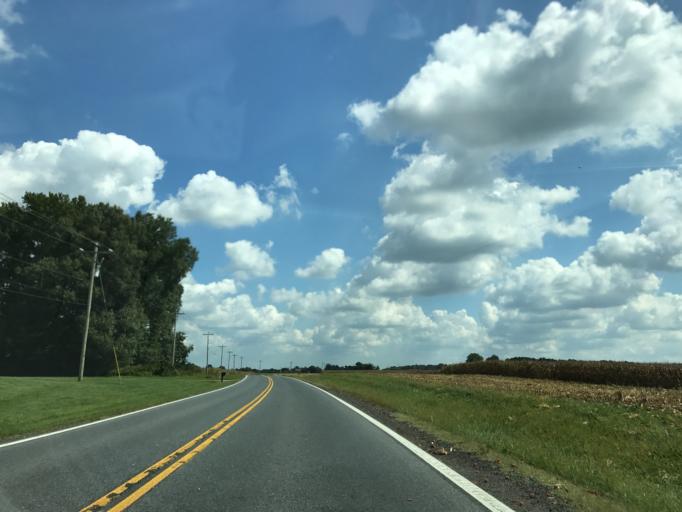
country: US
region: Maryland
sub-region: Caroline County
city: Ridgely
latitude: 39.0040
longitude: -75.9691
